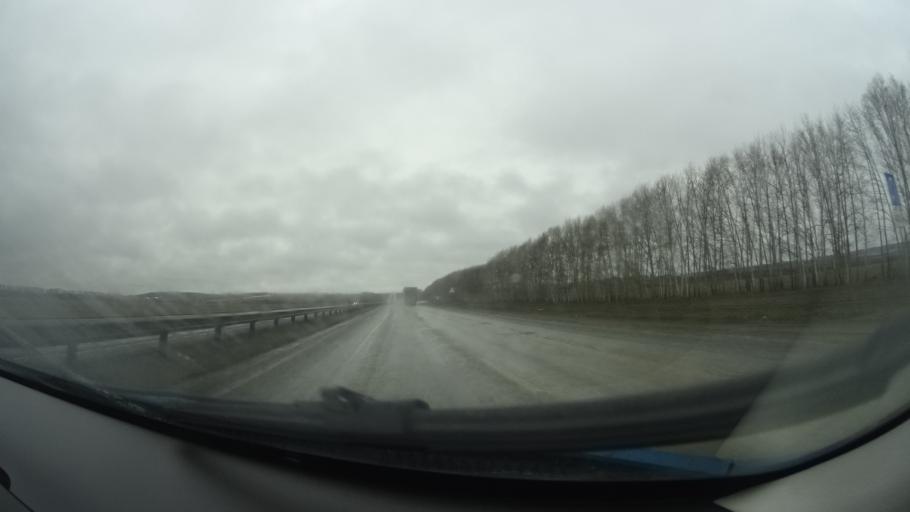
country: RU
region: Bashkortostan
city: Dmitriyevka
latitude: 54.6960
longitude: 55.2749
